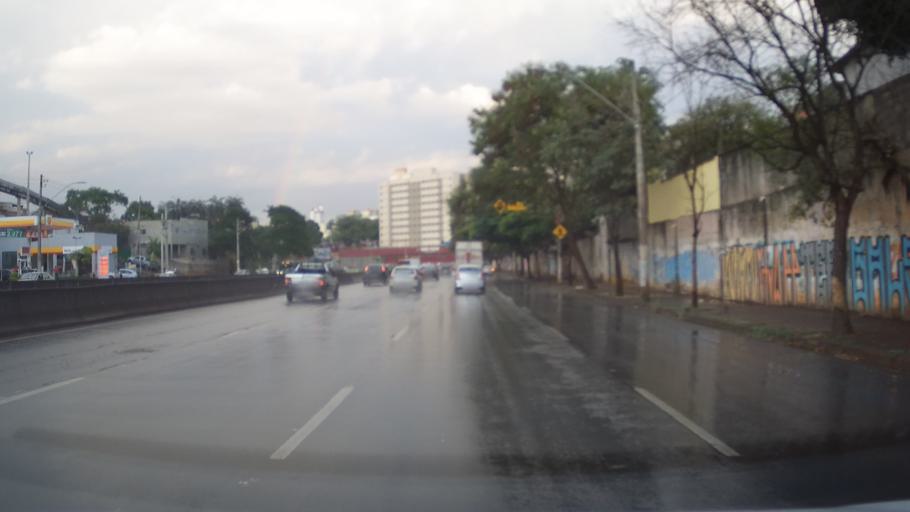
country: BR
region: Minas Gerais
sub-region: Belo Horizonte
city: Belo Horizonte
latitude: -19.9416
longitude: -43.9869
